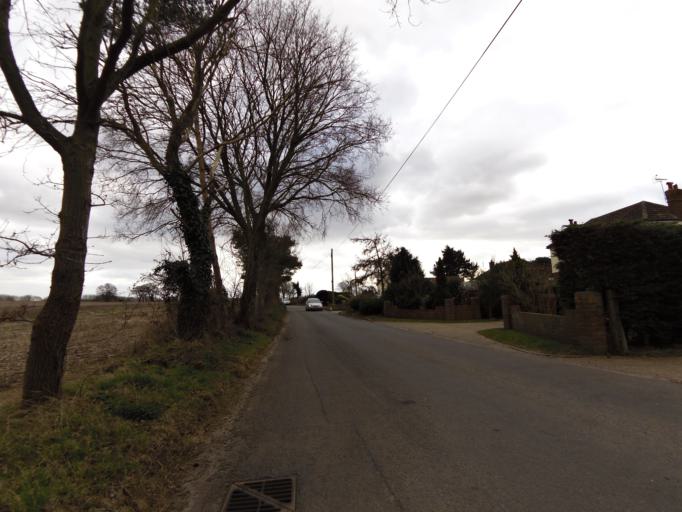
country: GB
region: England
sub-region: Suffolk
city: Shotley Gate
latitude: 52.0221
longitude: 1.2994
